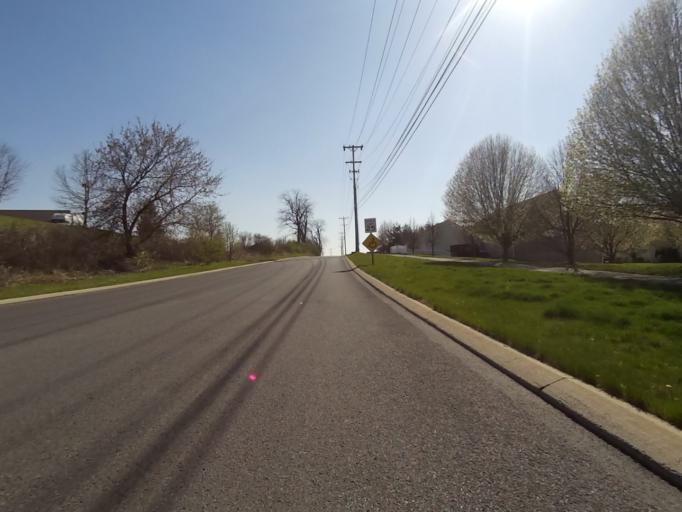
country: US
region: Pennsylvania
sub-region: Centre County
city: Houserville
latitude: 40.8357
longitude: -77.8073
